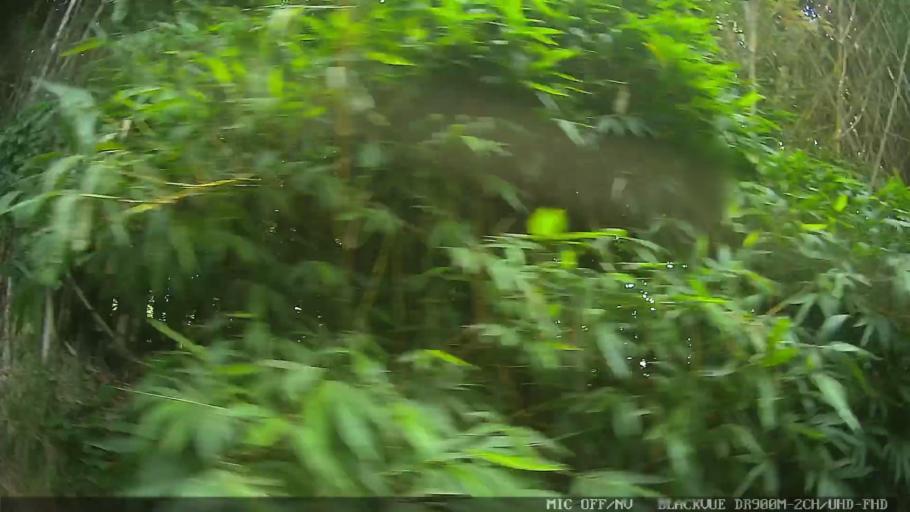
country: BR
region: Sao Paulo
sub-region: Atibaia
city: Atibaia
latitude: -23.1256
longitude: -46.6006
